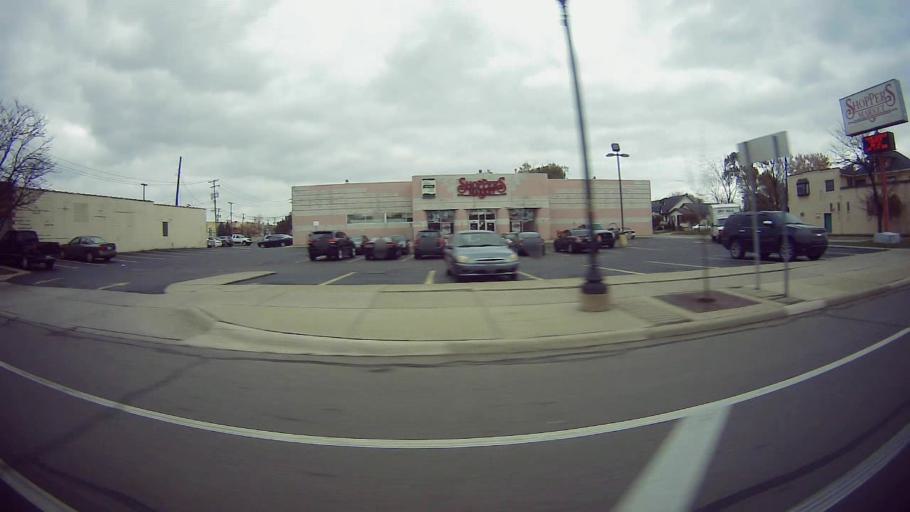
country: US
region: Michigan
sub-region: Macomb County
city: Warren
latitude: 42.4625
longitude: -83.0266
